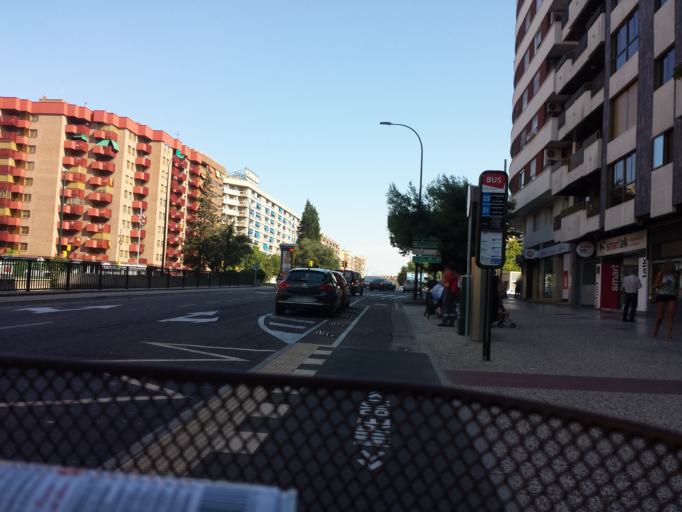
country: ES
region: Aragon
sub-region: Provincia de Zaragoza
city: Zaragoza
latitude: 41.6455
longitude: -0.8783
